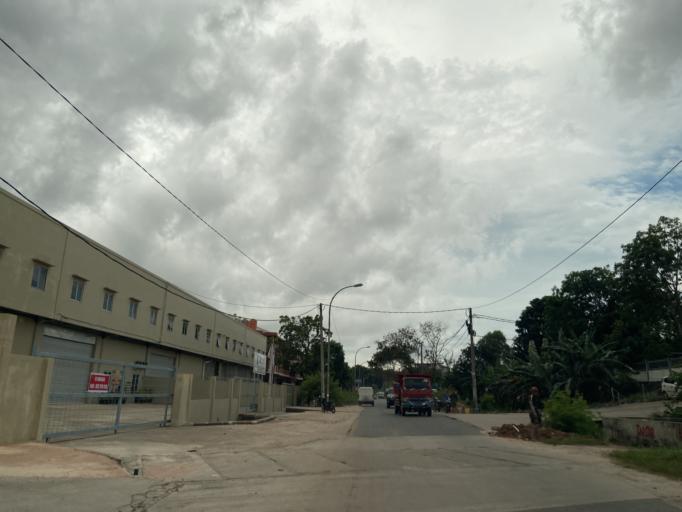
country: SG
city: Singapore
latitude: 1.1106
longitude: 104.0493
